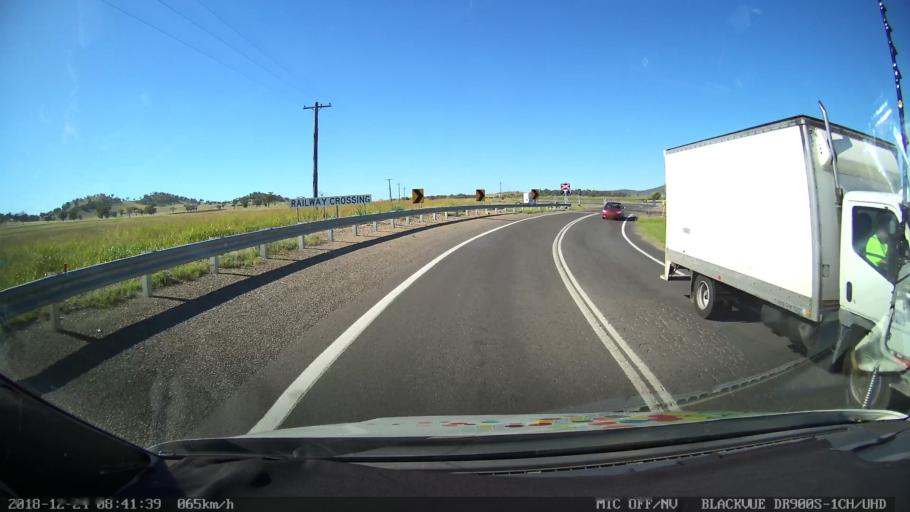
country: AU
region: New South Wales
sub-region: Liverpool Plains
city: Quirindi
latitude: -31.3654
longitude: 150.6450
